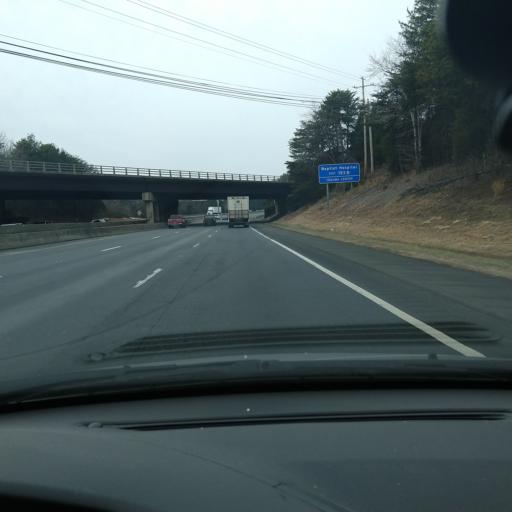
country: US
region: North Carolina
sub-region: Forsyth County
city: Winston-Salem
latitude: 36.0586
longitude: -80.2127
